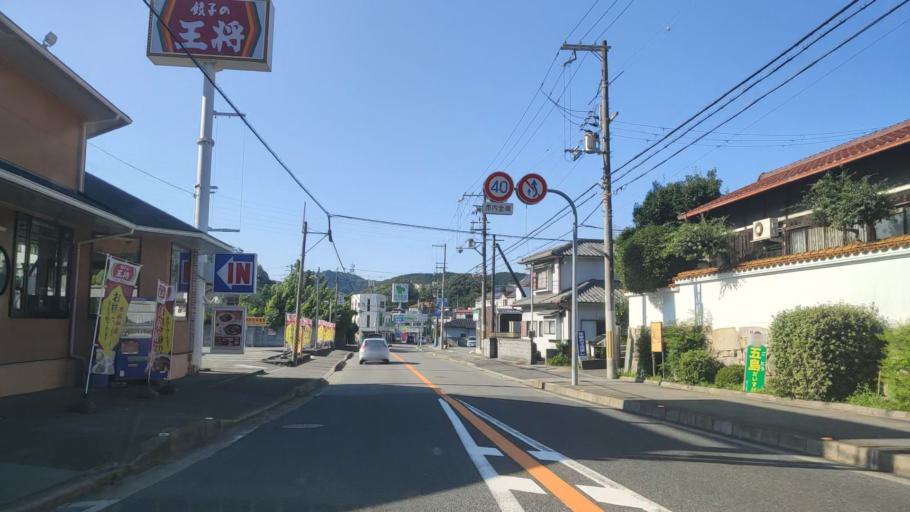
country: JP
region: Hyogo
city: Kobe
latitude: 34.7278
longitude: 135.1601
